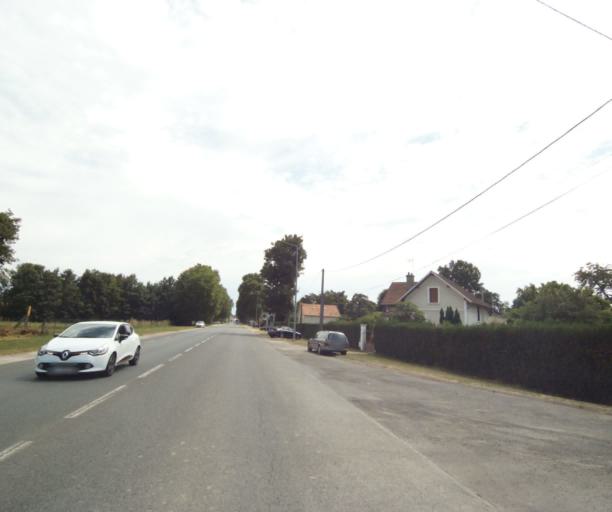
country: FR
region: Ile-de-France
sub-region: Departement de Seine-et-Marne
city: Chailly-en-Biere
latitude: 48.4712
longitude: 2.6029
